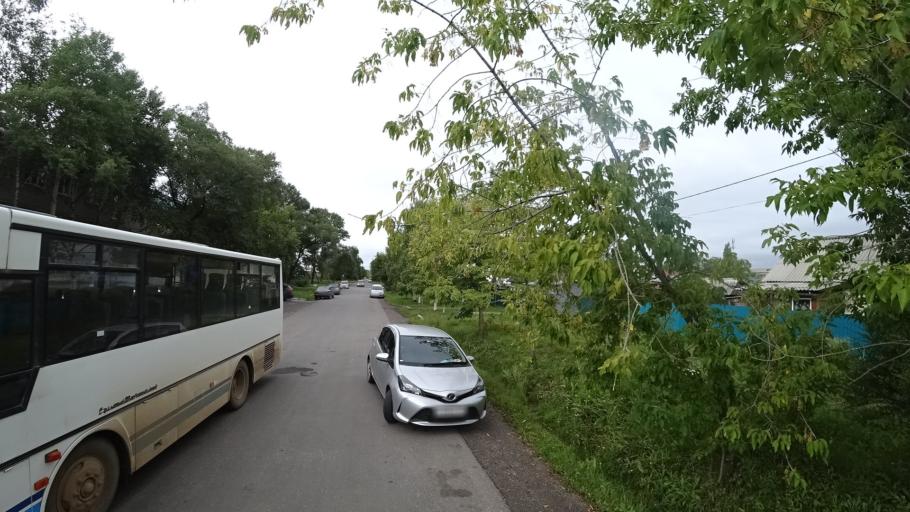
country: RU
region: Primorskiy
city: Chernigovka
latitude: 44.3385
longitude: 132.5809
